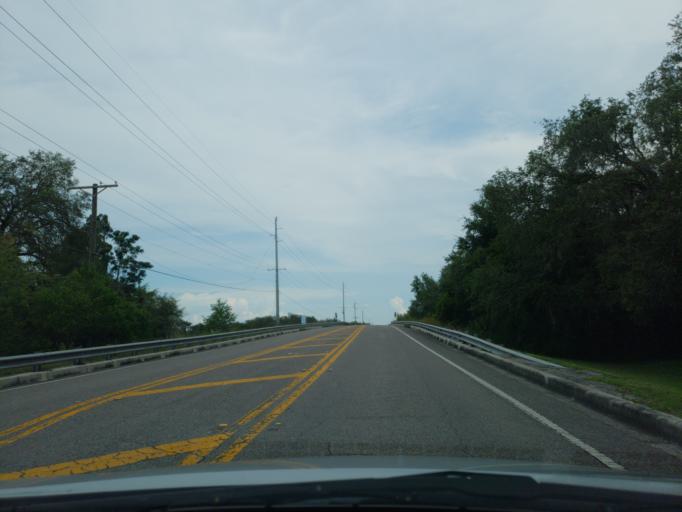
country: US
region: Florida
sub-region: Hillsborough County
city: University
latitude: 28.1089
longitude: -82.4308
